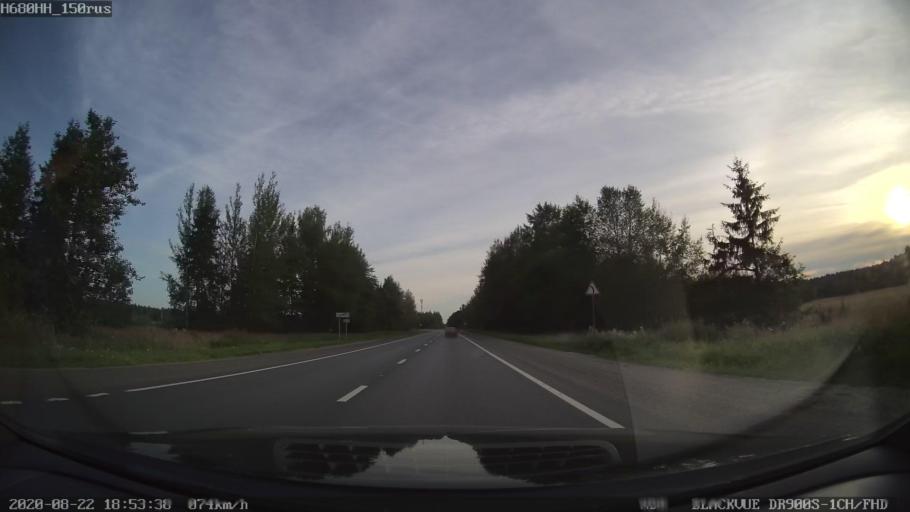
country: RU
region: Tverskaya
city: Rameshki
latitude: 57.2244
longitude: 36.0961
